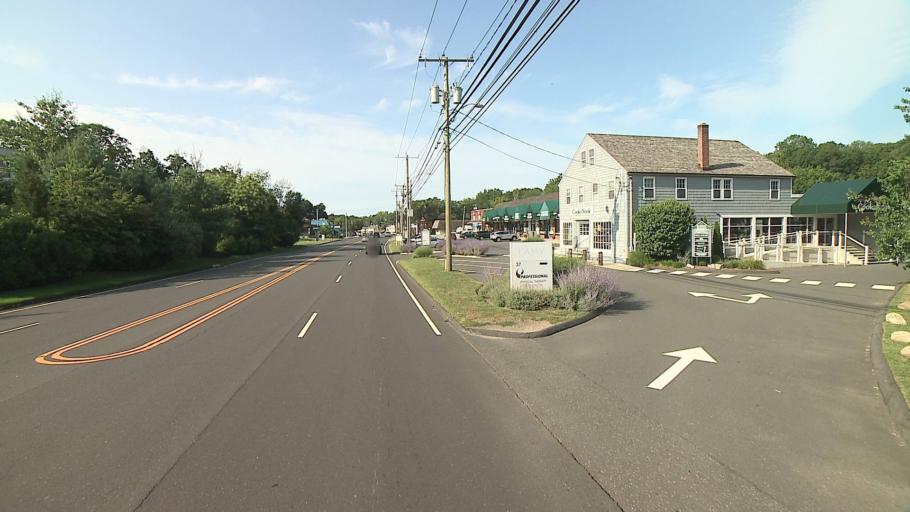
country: US
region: Connecticut
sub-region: Fairfield County
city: Wilton
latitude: 41.1660
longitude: -73.4177
